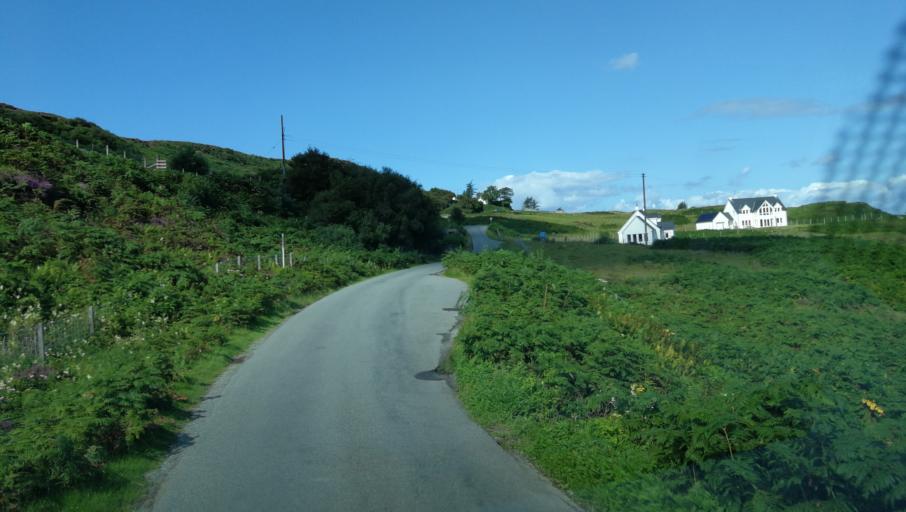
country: GB
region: Scotland
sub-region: Highland
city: Isle of Skye
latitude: 57.4490
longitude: -6.6520
